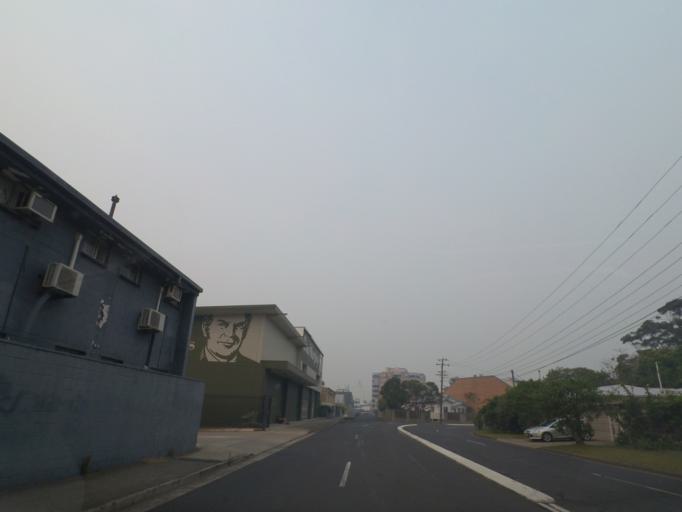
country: AU
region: New South Wales
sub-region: Coffs Harbour
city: Coffs Harbour
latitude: -30.2940
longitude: 153.1151
